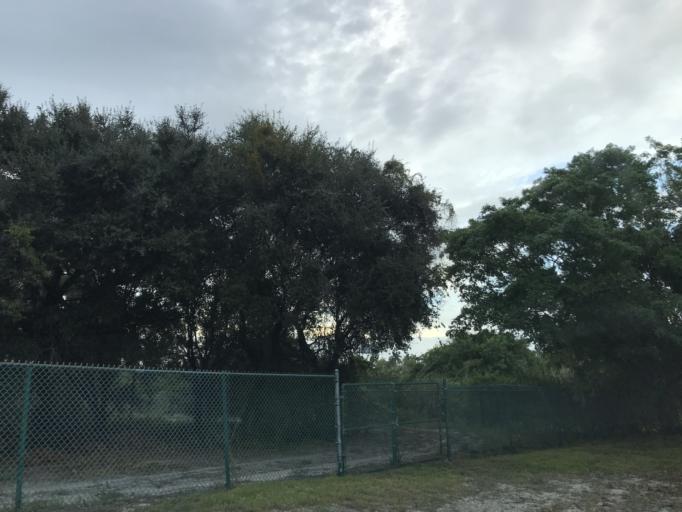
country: US
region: Florida
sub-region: Palm Beach County
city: Hypoluxo
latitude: 26.5652
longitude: -80.0710
